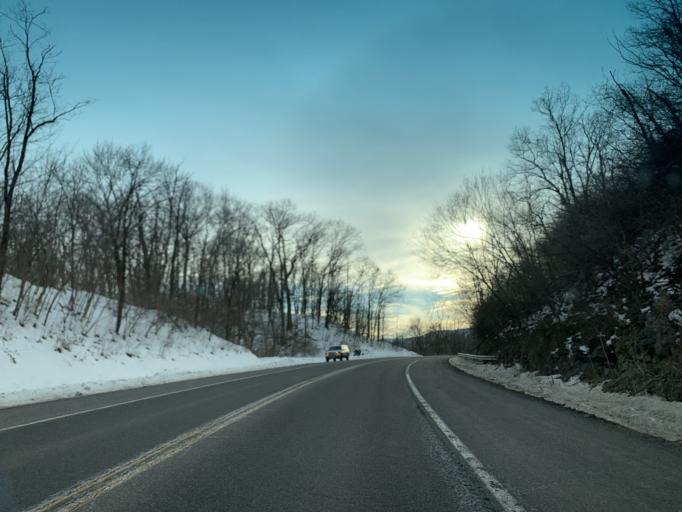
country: US
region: West Virginia
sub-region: Mineral County
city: Keyser
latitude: 39.4703
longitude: -78.9468
